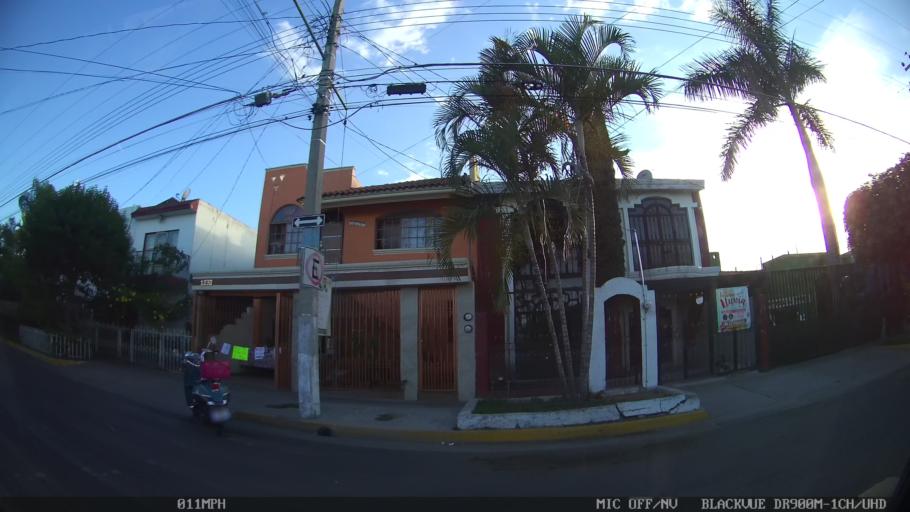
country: MX
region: Jalisco
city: Tlaquepaque
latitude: 20.7118
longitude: -103.3023
